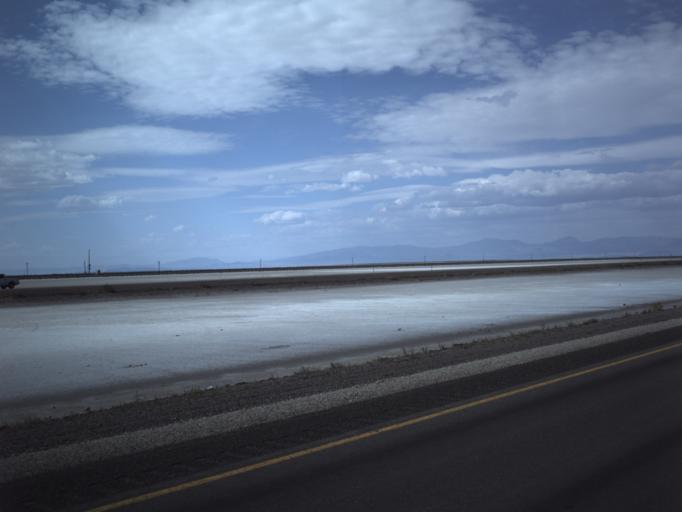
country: US
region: Utah
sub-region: Tooele County
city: Wendover
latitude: 40.7358
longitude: -113.6798
